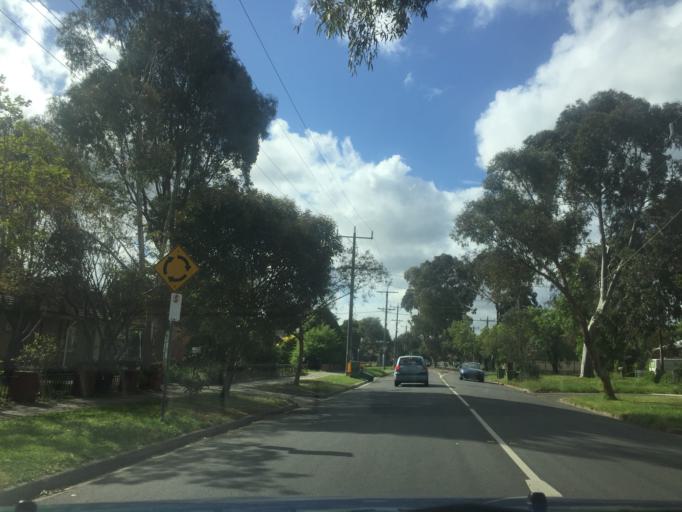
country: AU
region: Victoria
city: Heidelberg West
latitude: -37.7394
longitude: 145.0366
